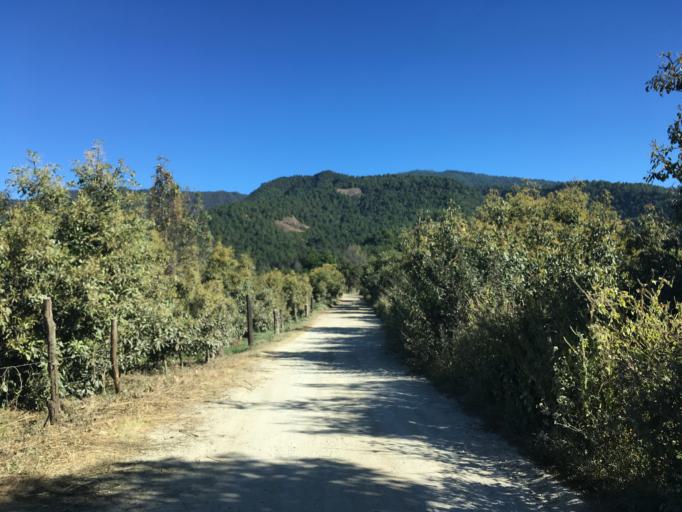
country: MX
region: Michoacan
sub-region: Zitacuaro
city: Macutzio
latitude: 19.4907
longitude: -100.3259
